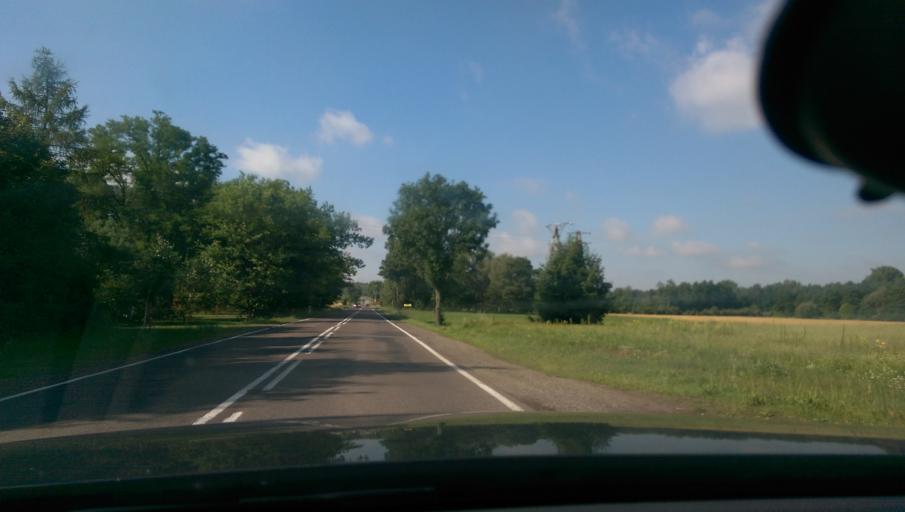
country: PL
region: Masovian Voivodeship
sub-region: Powiat plonski
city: Sochocin
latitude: 52.6836
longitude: 20.4634
